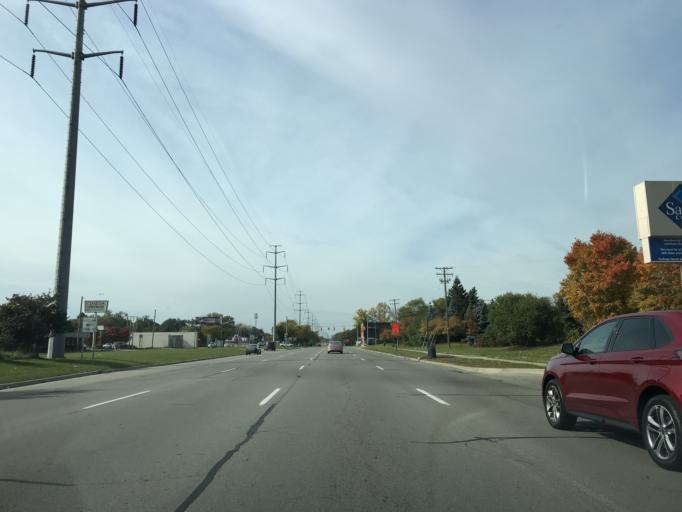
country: US
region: Michigan
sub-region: Oakland County
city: Southfield
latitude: 42.4435
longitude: -83.2643
